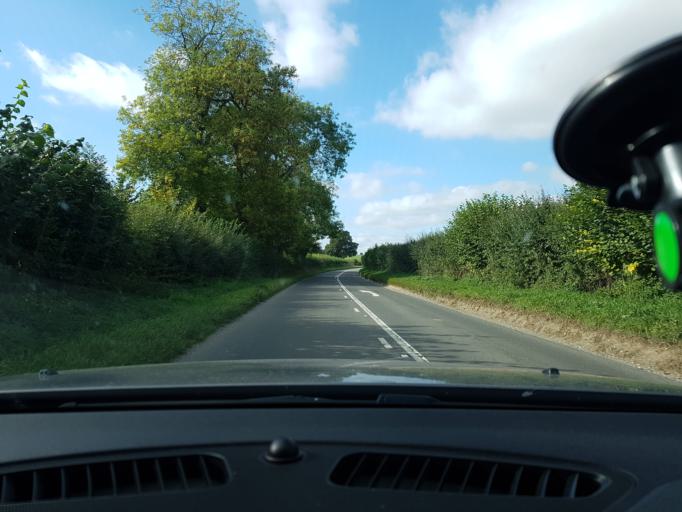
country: GB
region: England
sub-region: Wiltshire
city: Aldbourne
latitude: 51.4799
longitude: -1.6273
